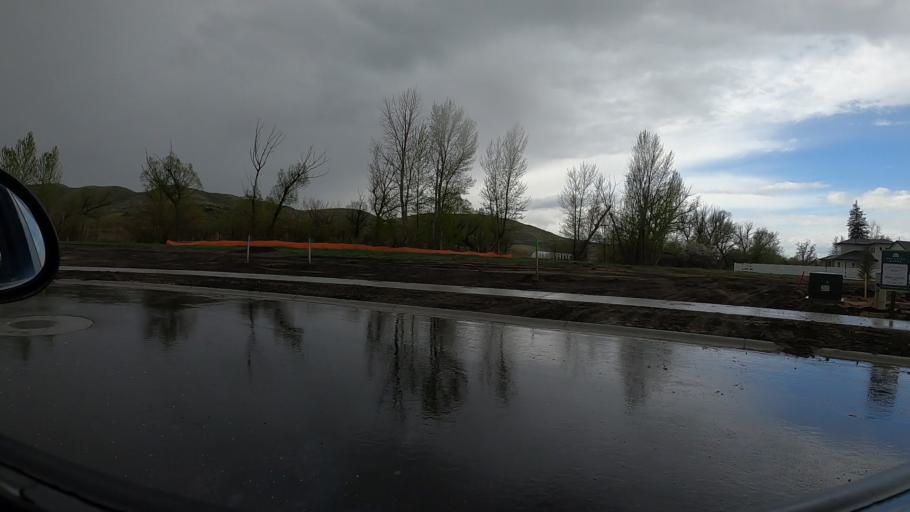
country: US
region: Idaho
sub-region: Ada County
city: Eagle
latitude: 43.7312
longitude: -116.2869
